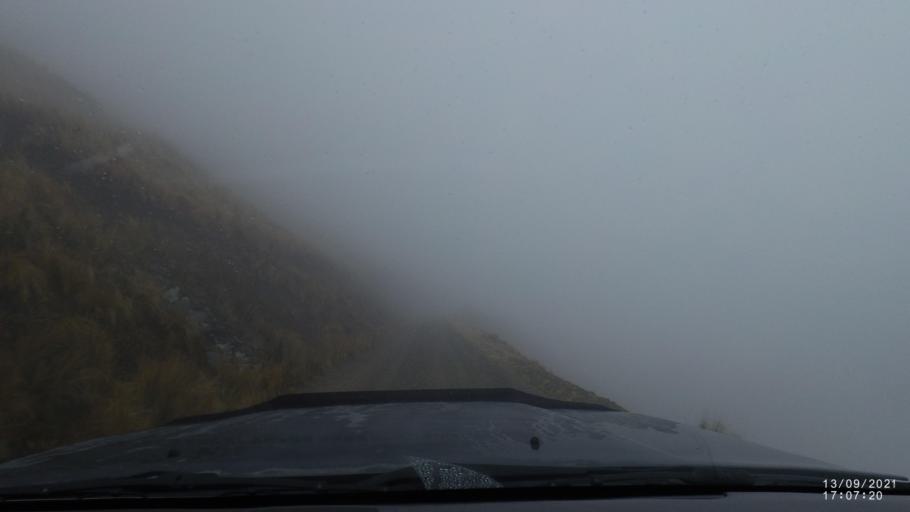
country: BO
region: Cochabamba
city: Colomi
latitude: -17.3287
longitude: -65.7248
